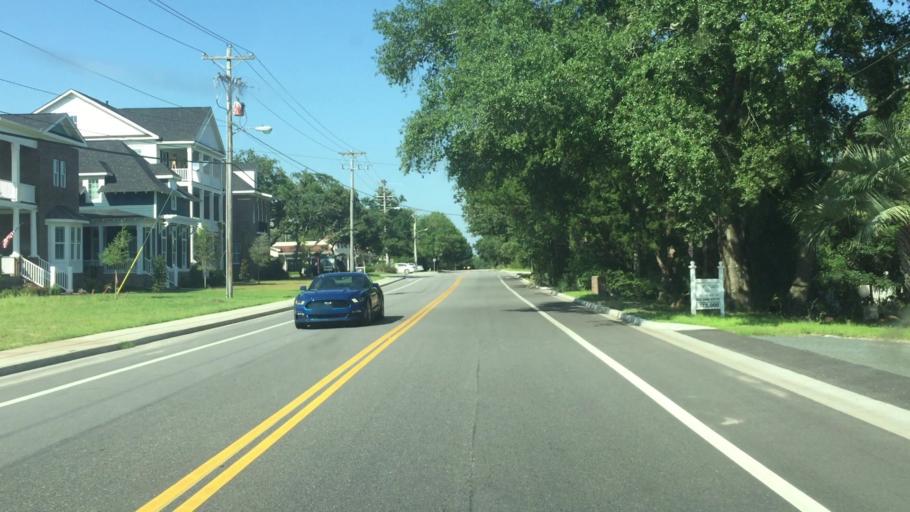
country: US
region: South Carolina
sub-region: Horry County
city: Myrtle Beach
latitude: 33.7461
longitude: -78.8142
